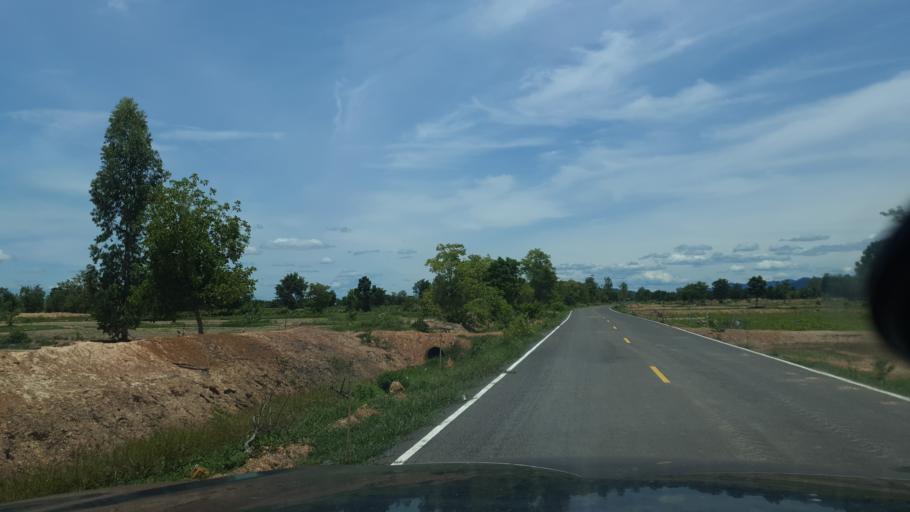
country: TH
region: Sukhothai
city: Ban Na
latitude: 17.1506
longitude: 99.6497
